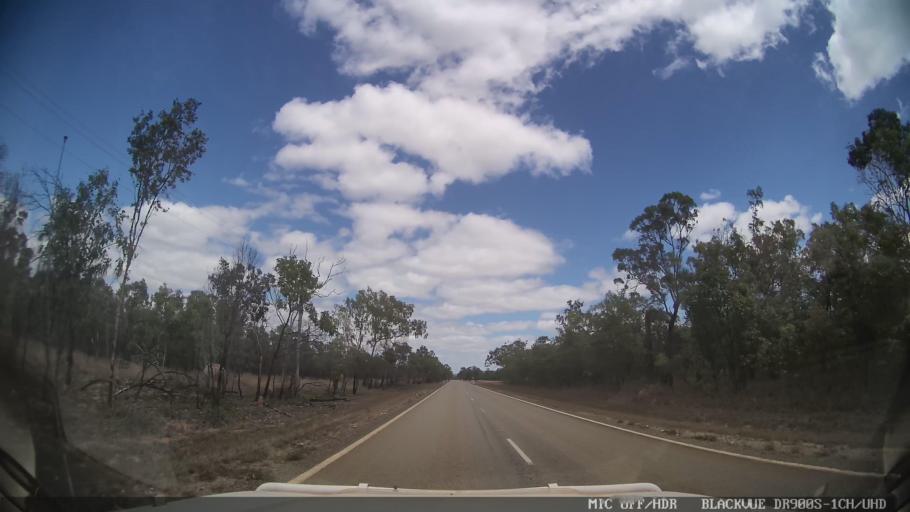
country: AU
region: Queensland
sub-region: Tablelands
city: Ravenshoe
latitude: -17.8156
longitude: 144.9563
